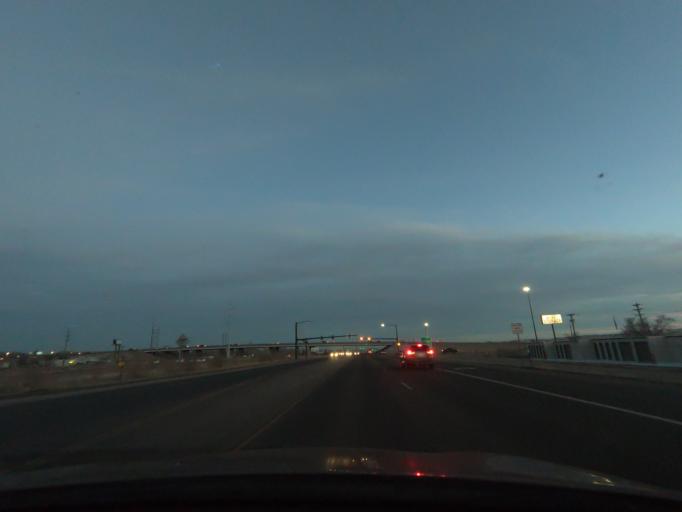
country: US
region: Colorado
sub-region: El Paso County
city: Stratmoor
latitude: 38.7700
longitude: -104.7630
